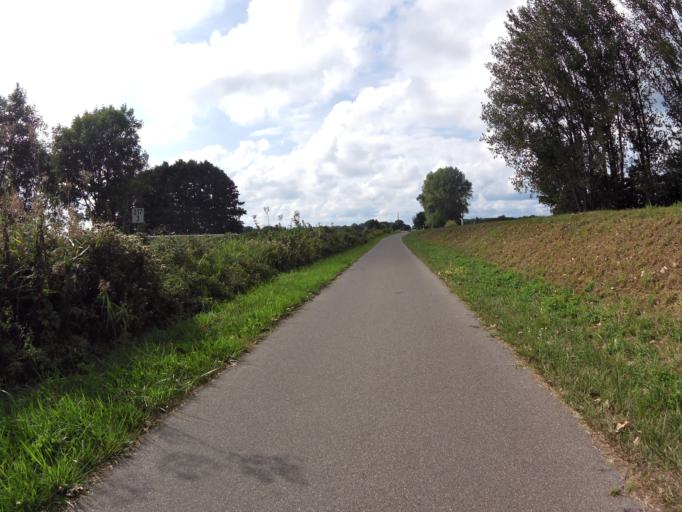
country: DE
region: Mecklenburg-Vorpommern
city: Seebad Bansin
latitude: 53.9802
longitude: 14.0919
